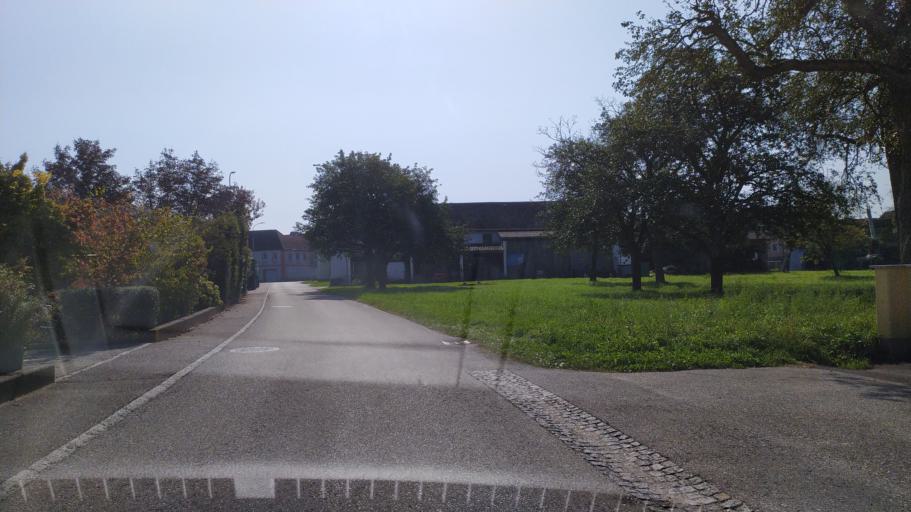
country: AT
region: Lower Austria
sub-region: Politischer Bezirk Amstetten
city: Strengberg
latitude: 48.1867
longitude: 14.7082
